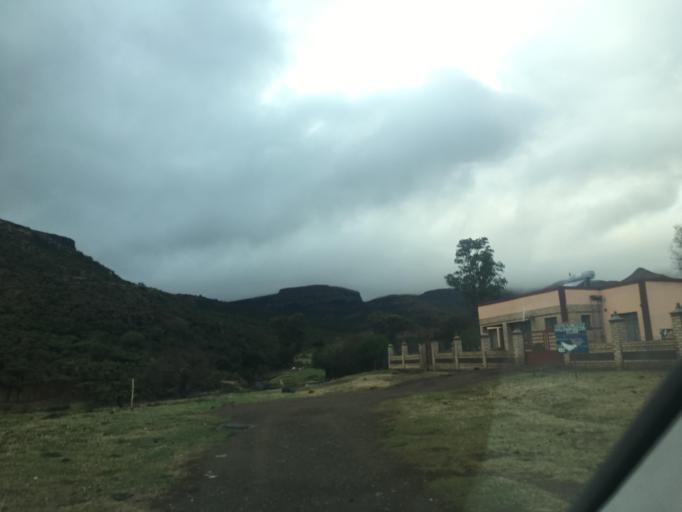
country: ZA
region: Eastern Cape
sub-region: Chris Hani District Municipality
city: Cala
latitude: -31.5226
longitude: 27.7041
